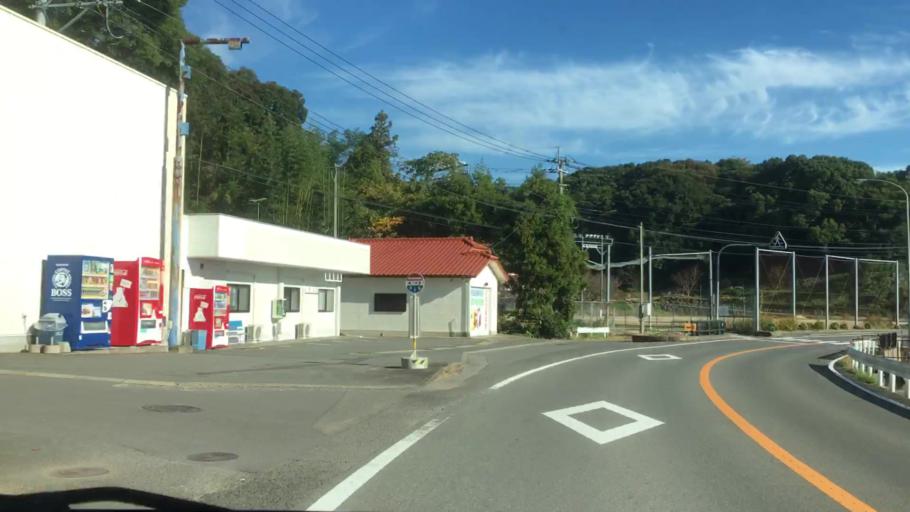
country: JP
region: Nagasaki
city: Sasebo
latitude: 33.0165
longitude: 129.7328
